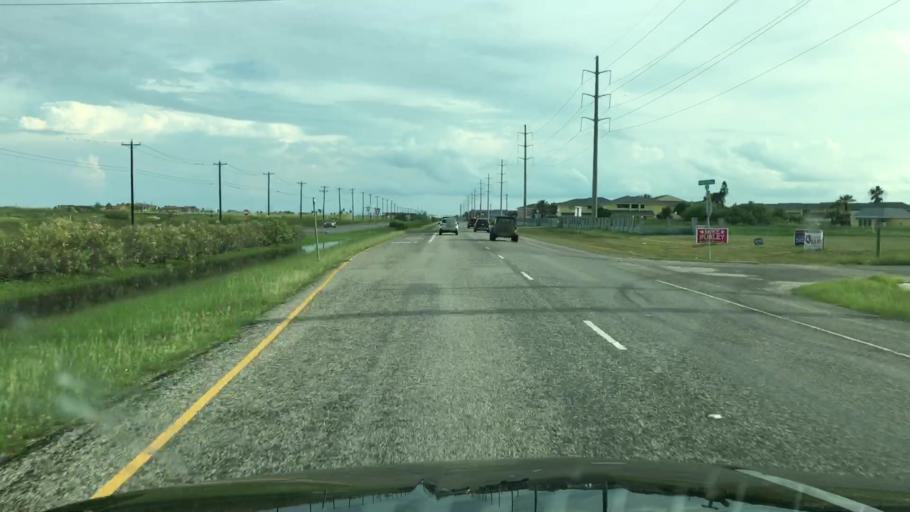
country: US
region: Texas
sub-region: Nueces County
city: Corpus Christi
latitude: 27.6145
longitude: -97.2219
